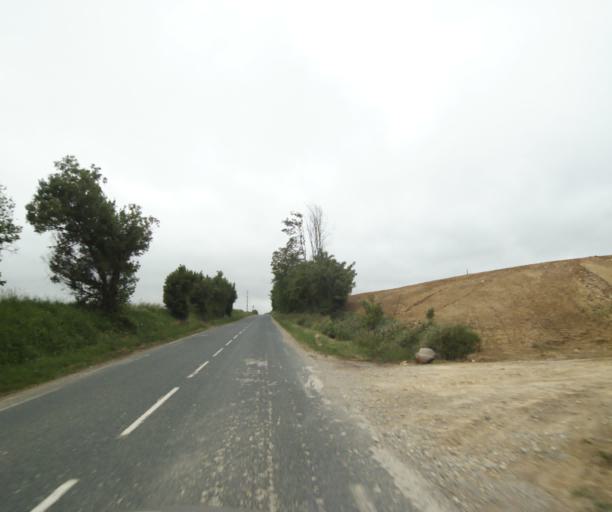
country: FR
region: Rhone-Alpes
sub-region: Departement de l'Ain
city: Miribel
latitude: 45.8523
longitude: 4.9311
